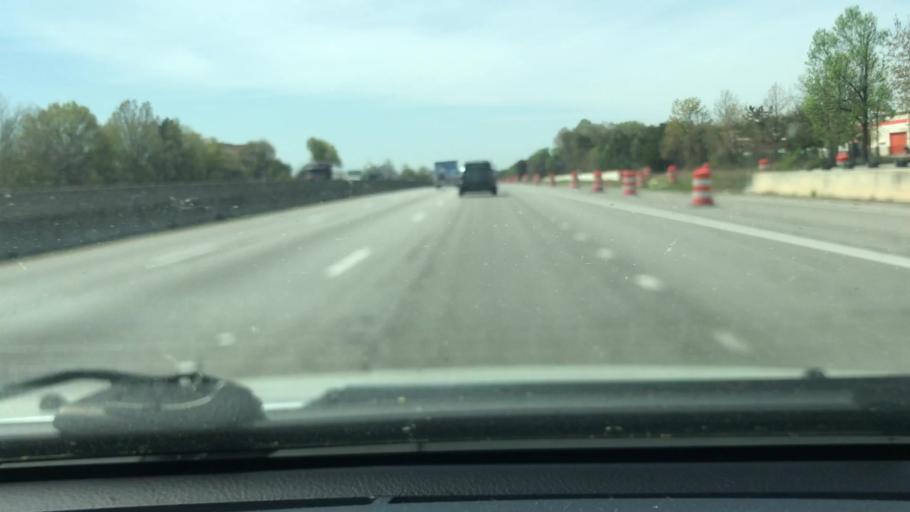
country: US
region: South Carolina
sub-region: Greenville County
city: Mauldin
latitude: 34.8283
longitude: -82.3051
